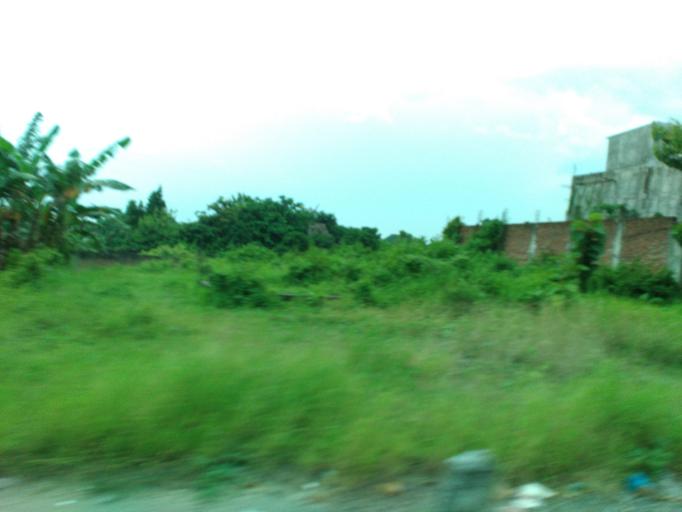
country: ID
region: Central Java
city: Gatak
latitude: -7.5908
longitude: 110.7051
